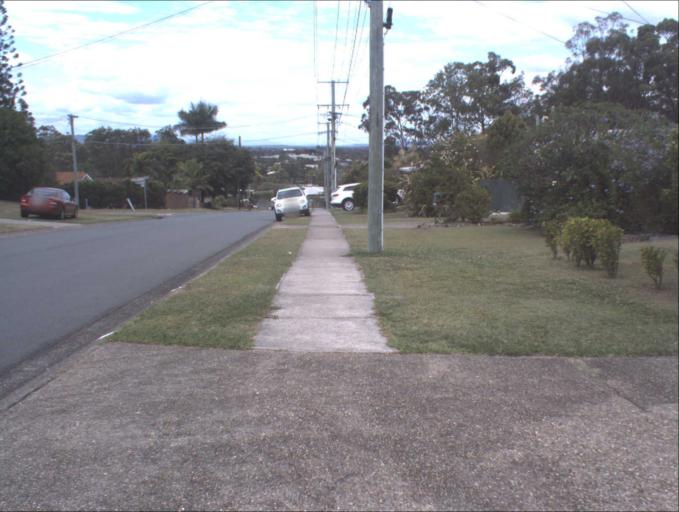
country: AU
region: Queensland
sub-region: Logan
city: Slacks Creek
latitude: -27.6302
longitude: 153.1457
